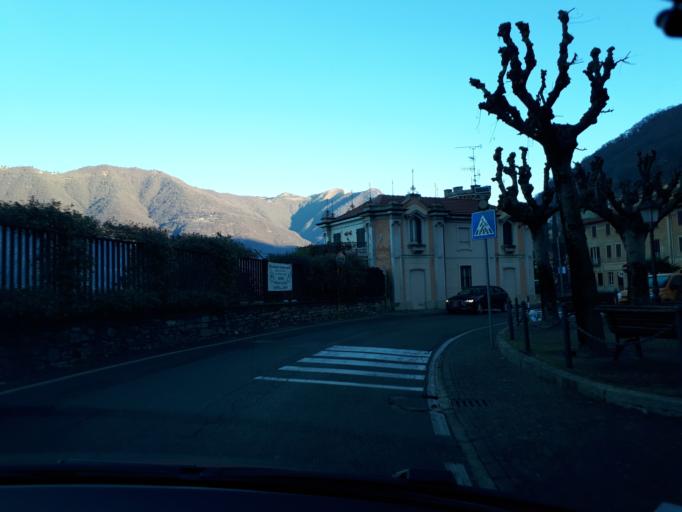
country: IT
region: Lombardy
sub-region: Provincia di Como
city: Blevio
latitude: 45.8378
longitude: 9.1019
